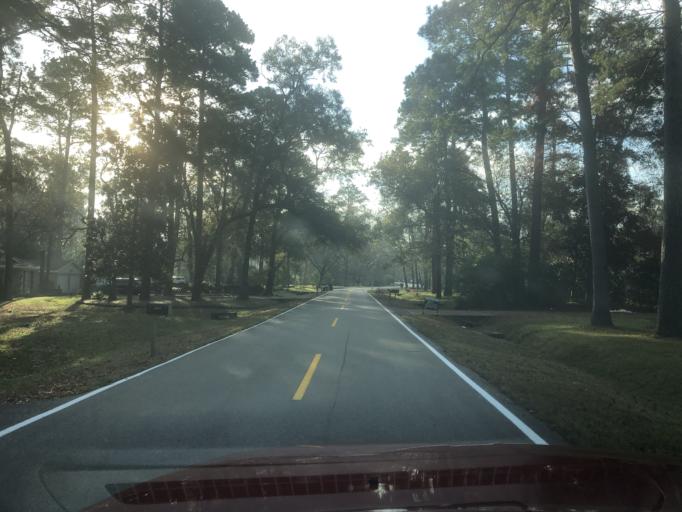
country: US
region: Texas
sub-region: Harris County
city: Spring
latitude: 30.0143
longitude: -95.4772
